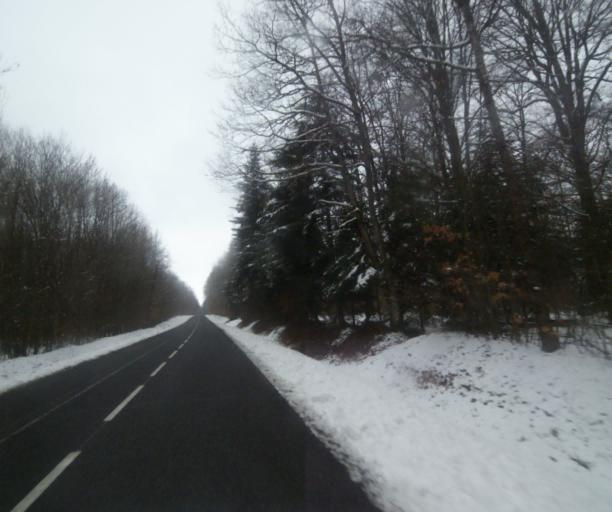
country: FR
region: Champagne-Ardenne
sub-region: Departement de la Haute-Marne
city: Laneuville-a-Remy
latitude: 48.4480
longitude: 4.8647
